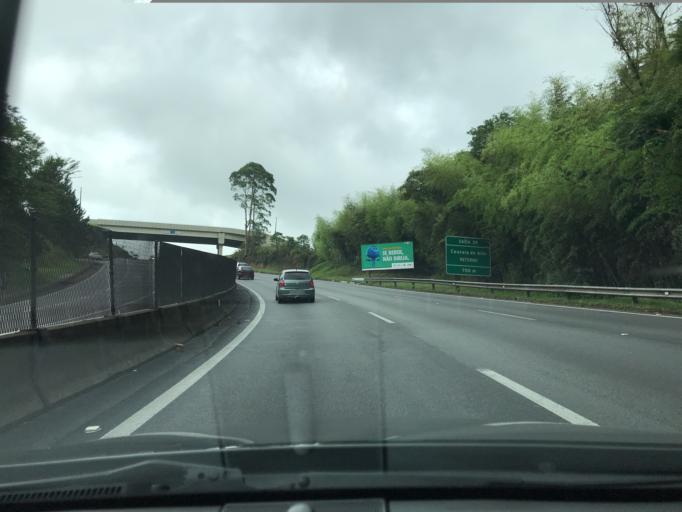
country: BR
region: Sao Paulo
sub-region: Cotia
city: Cotia
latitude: -23.6149
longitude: -46.9656
